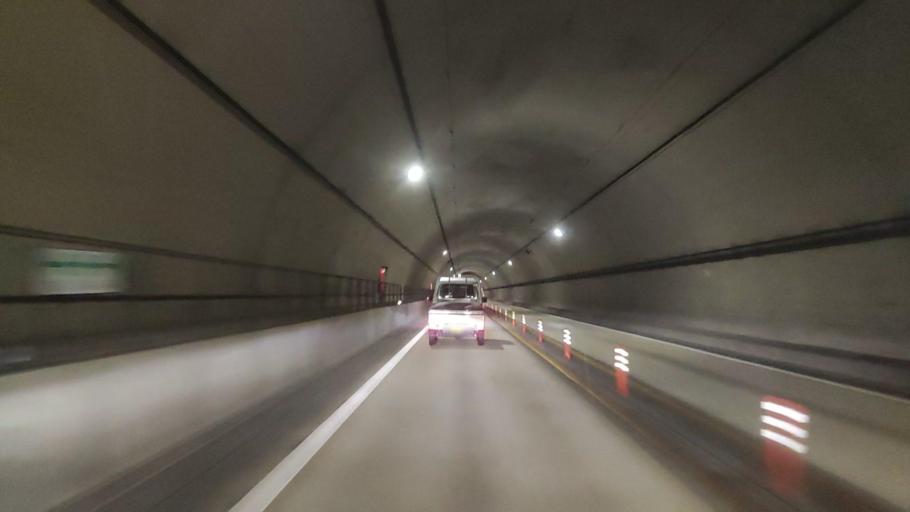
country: JP
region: Wakayama
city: Tanabe
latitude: 33.6085
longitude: 135.4274
